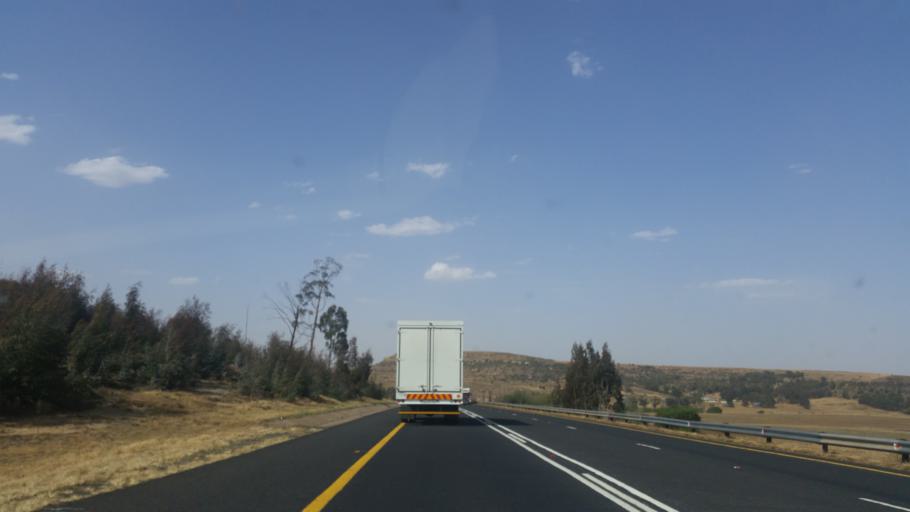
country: ZA
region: Orange Free State
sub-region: Thabo Mofutsanyana District Municipality
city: Bethlehem
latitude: -28.2963
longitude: 28.5918
